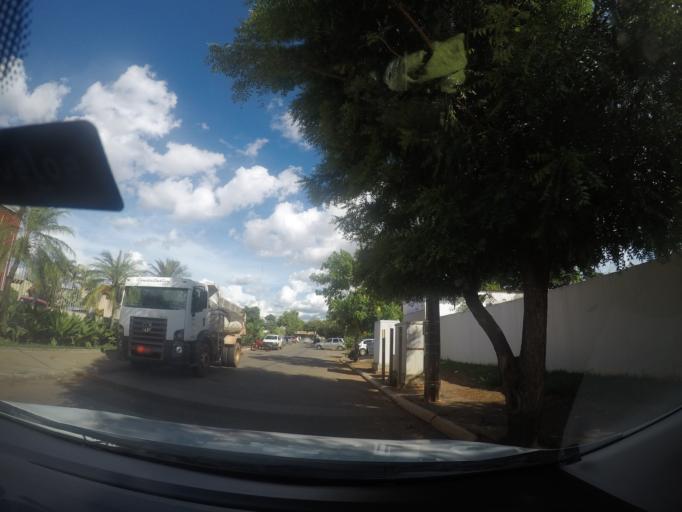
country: BR
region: Goias
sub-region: Goiania
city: Goiania
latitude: -16.6783
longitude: -49.2986
